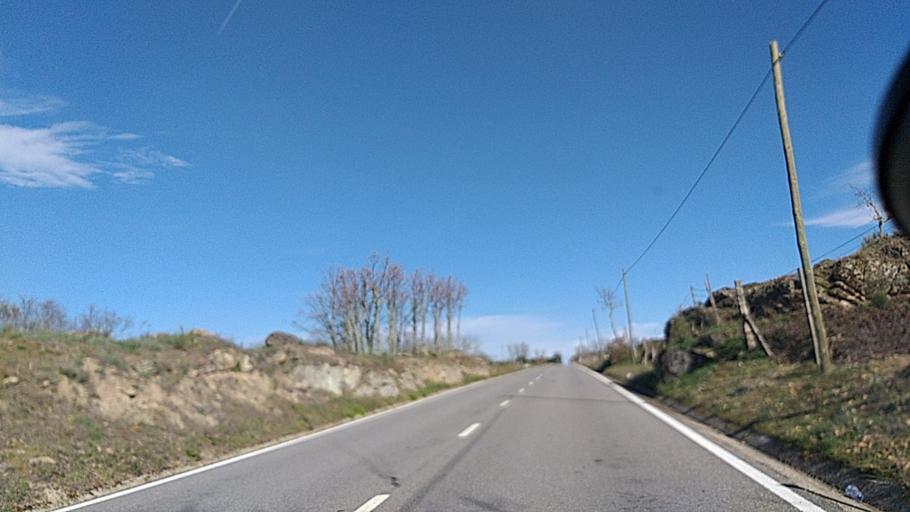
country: ES
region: Castille and Leon
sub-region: Provincia de Salamanca
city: Fuentes de Onoro
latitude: 40.6155
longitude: -6.8674
